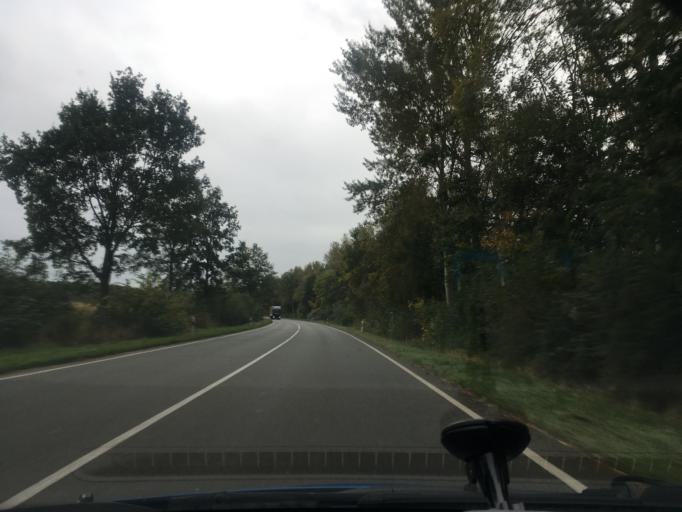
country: DE
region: Lower Saxony
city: Marschacht
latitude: 53.4140
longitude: 10.3335
